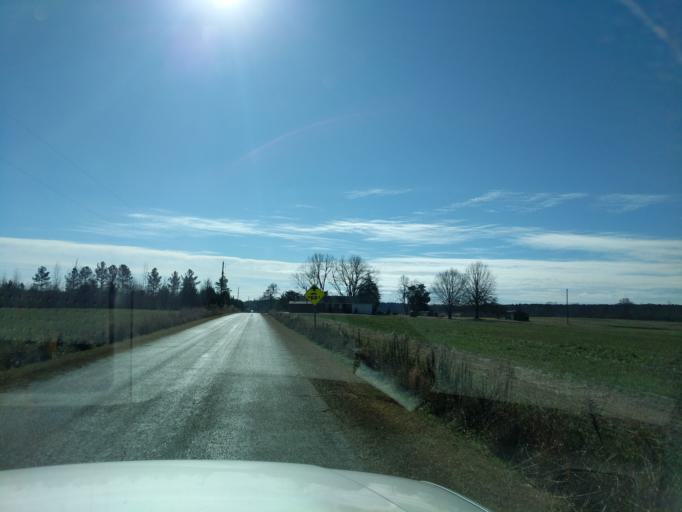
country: US
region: South Carolina
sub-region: Saluda County
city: Saluda
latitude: 34.0168
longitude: -81.8470
